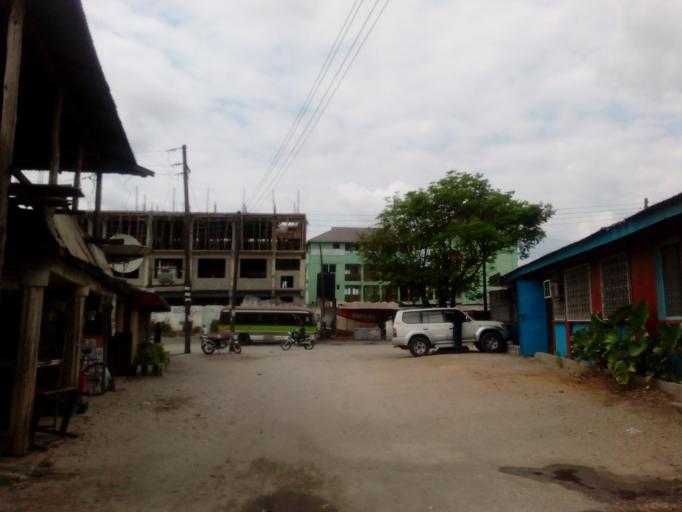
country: TZ
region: Dar es Salaam
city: Dar es Salaam
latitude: -6.8553
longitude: 39.2559
